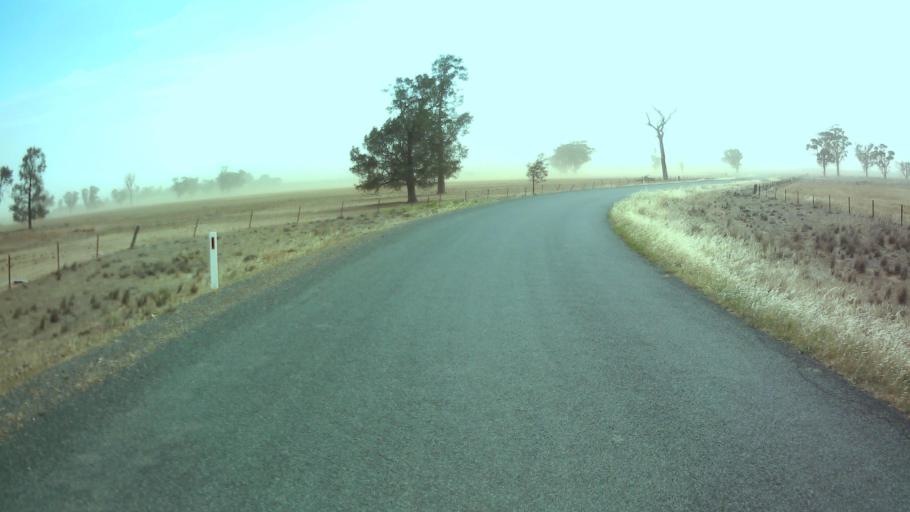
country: AU
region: New South Wales
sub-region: Weddin
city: Grenfell
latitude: -33.7374
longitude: 147.9936
